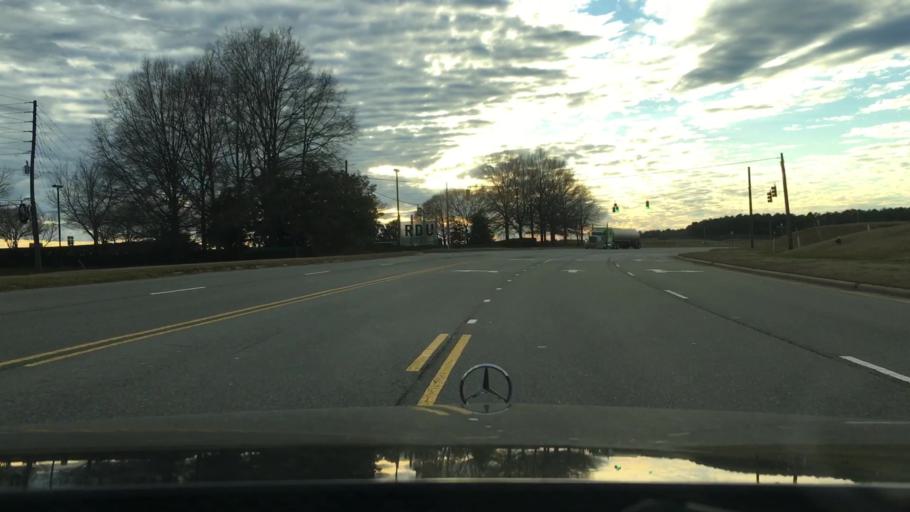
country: US
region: North Carolina
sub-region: Wake County
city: Morrisville
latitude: 35.8984
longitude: -78.7707
